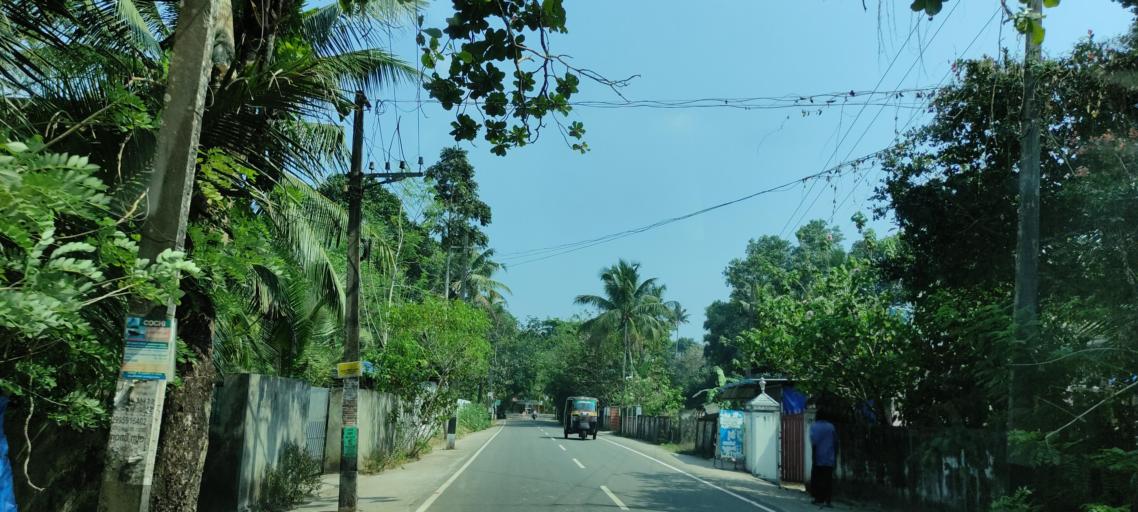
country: IN
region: Kerala
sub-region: Alappuzha
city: Shertallai
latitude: 9.6009
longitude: 76.3270
